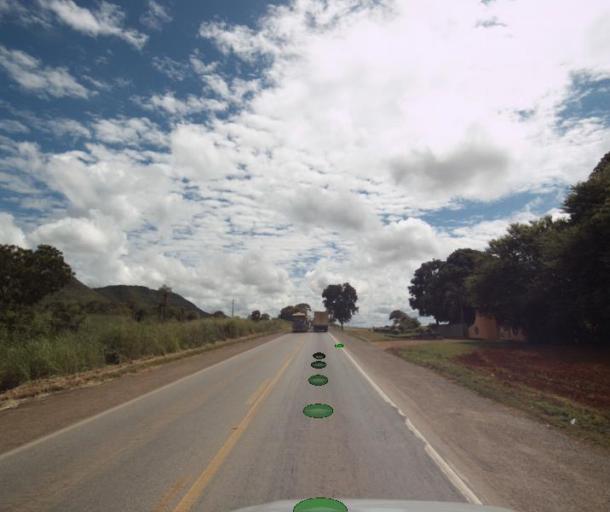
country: BR
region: Goias
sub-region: Uruacu
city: Uruacu
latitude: -14.4034
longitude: -49.1575
